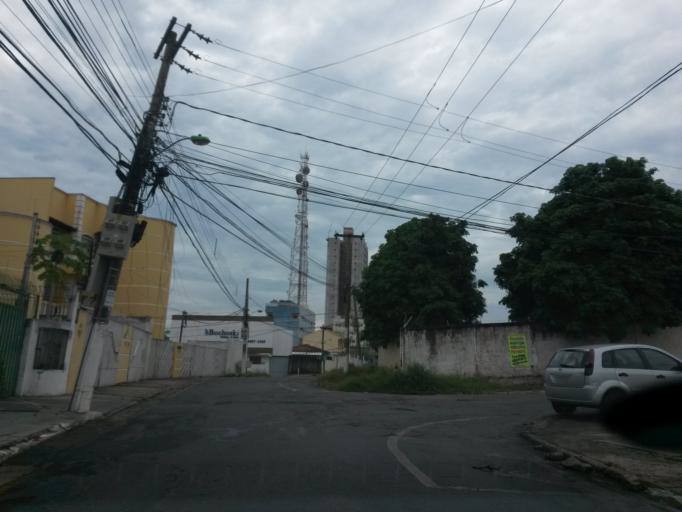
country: BR
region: Mato Grosso
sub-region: Cuiaba
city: Cuiaba
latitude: -15.6043
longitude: -56.0800
